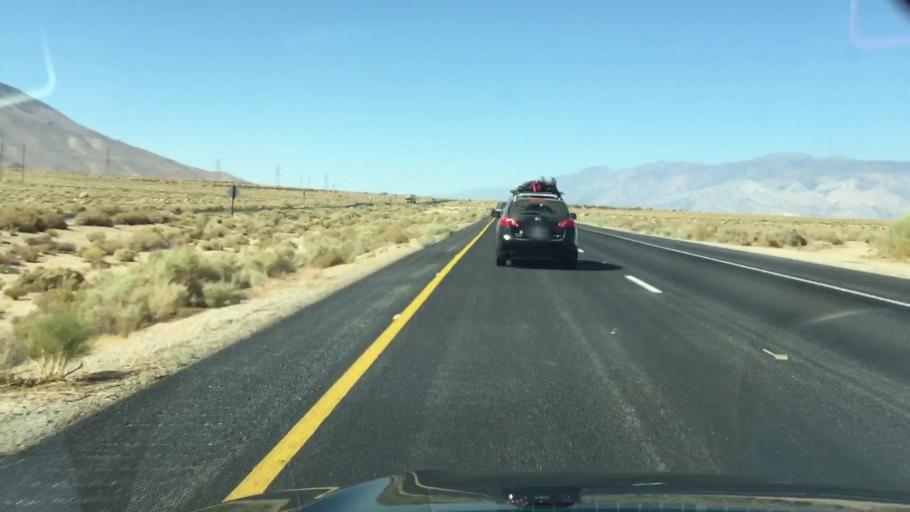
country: US
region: California
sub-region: Inyo County
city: Lone Pine
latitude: 36.3806
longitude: -118.0236
